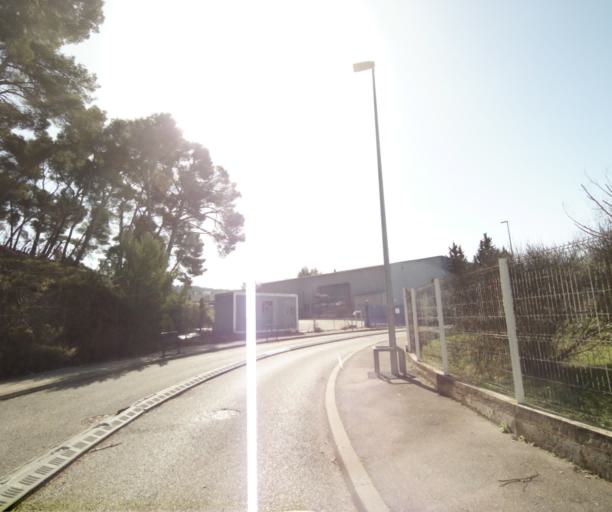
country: FR
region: Provence-Alpes-Cote d'Azur
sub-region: Departement des Bouches-du-Rhone
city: Cabries
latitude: 43.4277
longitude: 5.3948
